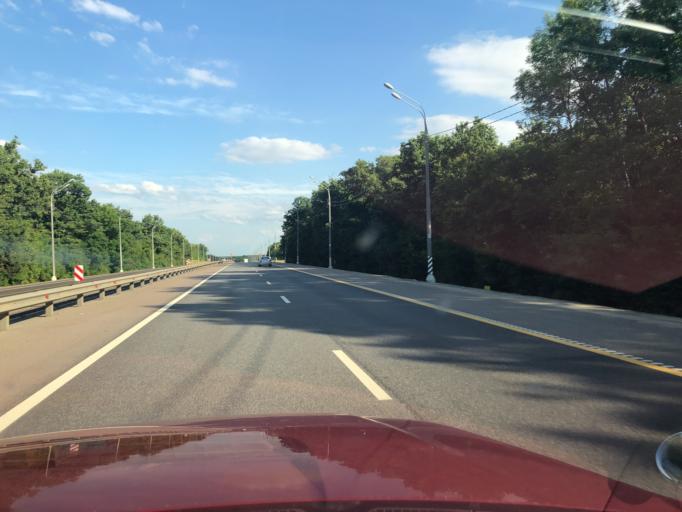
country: RU
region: Lipetsk
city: Zadonsk
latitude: 52.4157
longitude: 38.8425
